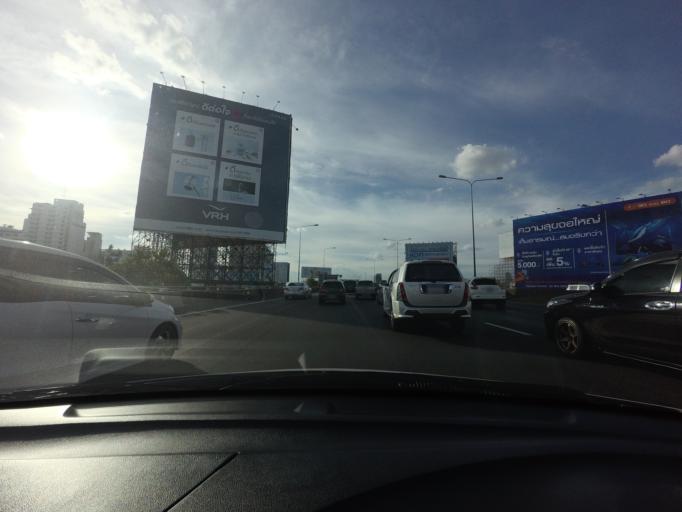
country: TH
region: Bangkok
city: Din Daeng
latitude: 13.7601
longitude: 100.5466
